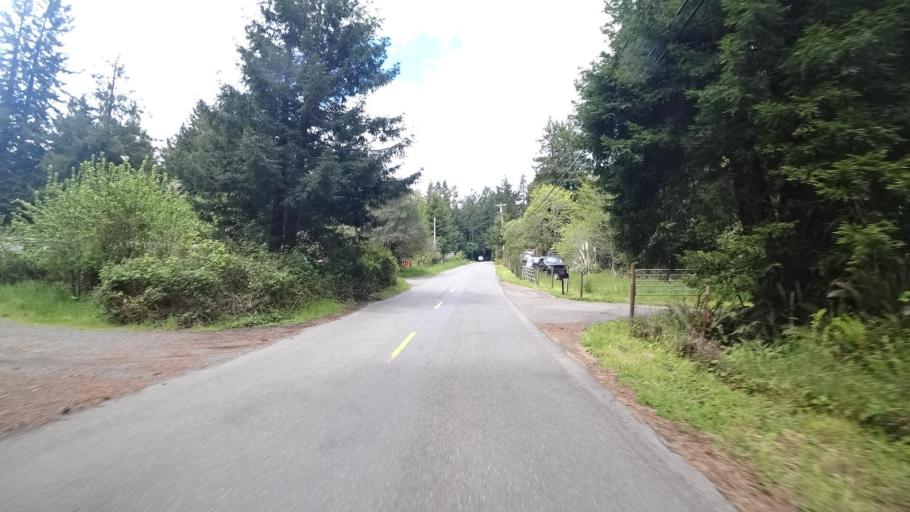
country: US
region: California
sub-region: Humboldt County
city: Bayside
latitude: 40.7973
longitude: -124.0501
